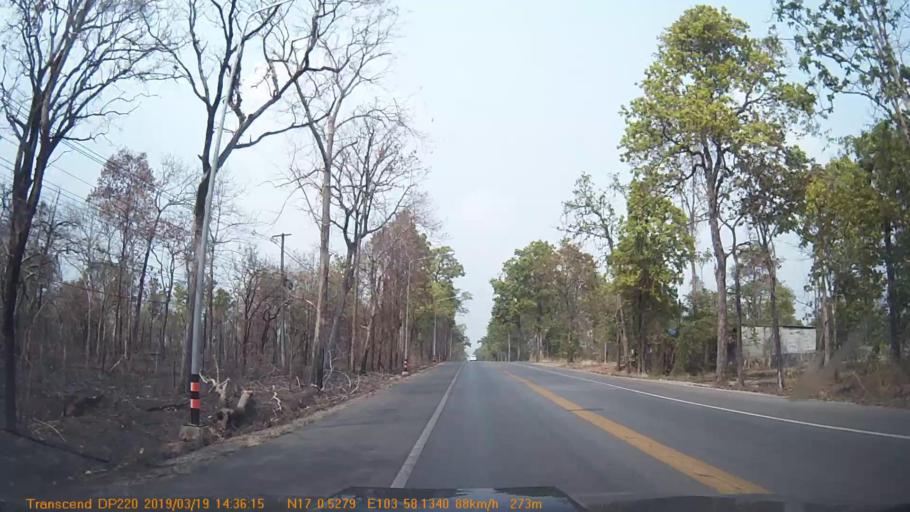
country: TH
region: Sakon Nakhon
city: Phu Phan
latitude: 17.0090
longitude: 103.9690
